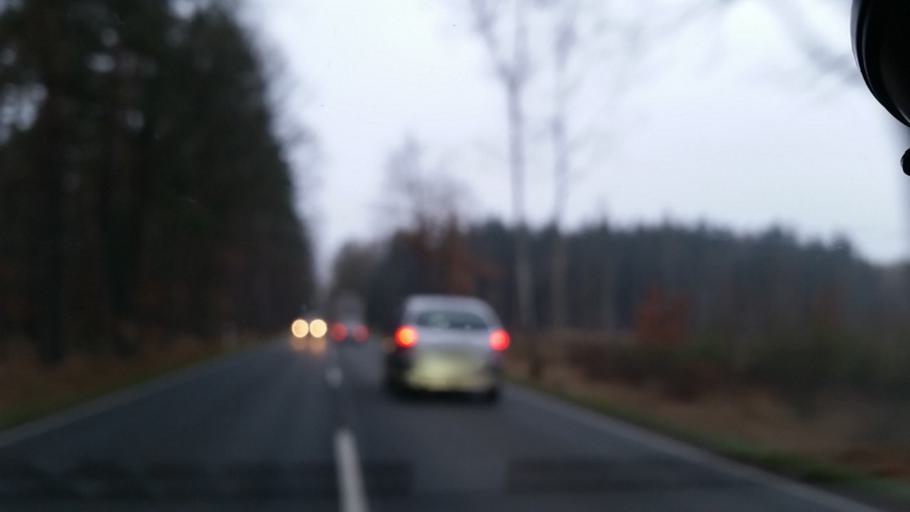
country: DE
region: Lower Saxony
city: Barwedel
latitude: 52.5474
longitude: 10.7844
